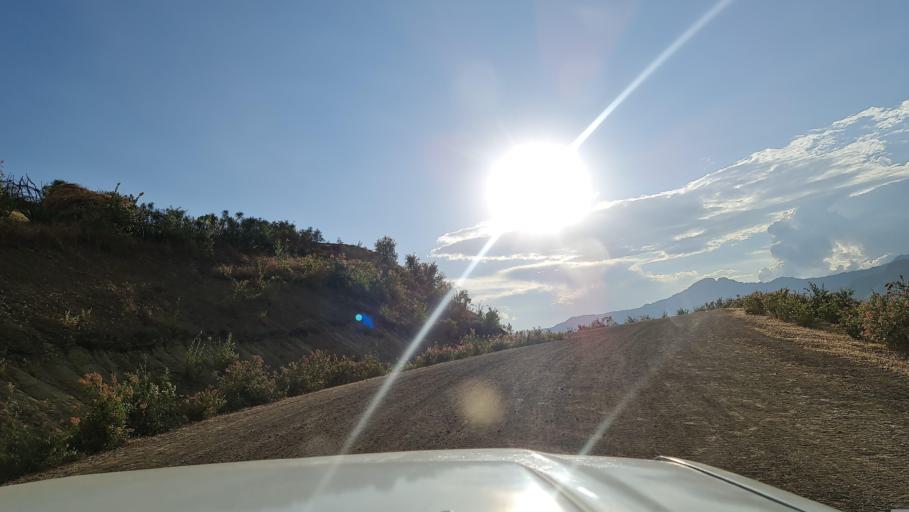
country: ET
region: Amhara
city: Debark'
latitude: 13.0571
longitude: 38.0188
